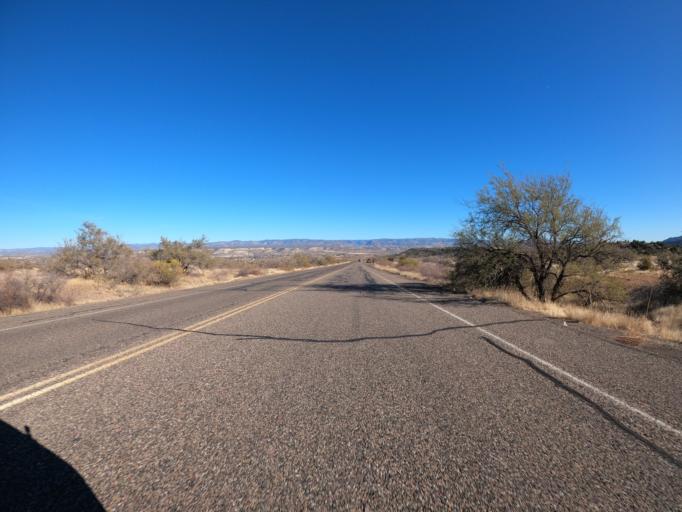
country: US
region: Arizona
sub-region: Yavapai County
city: Camp Verde
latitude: 34.5590
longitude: -111.9014
